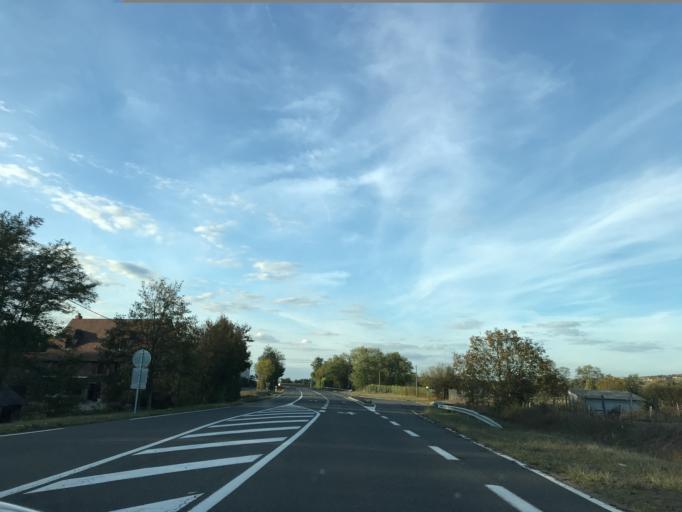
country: FR
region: Auvergne
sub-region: Departement de l'Allier
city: Saint-Yorre
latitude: 46.0402
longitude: 3.4744
